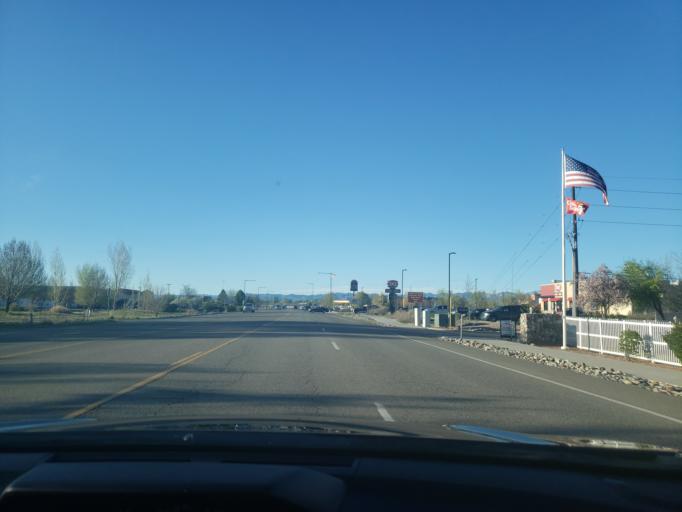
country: US
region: Colorado
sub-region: Mesa County
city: Fruita
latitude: 39.1494
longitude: -108.7382
